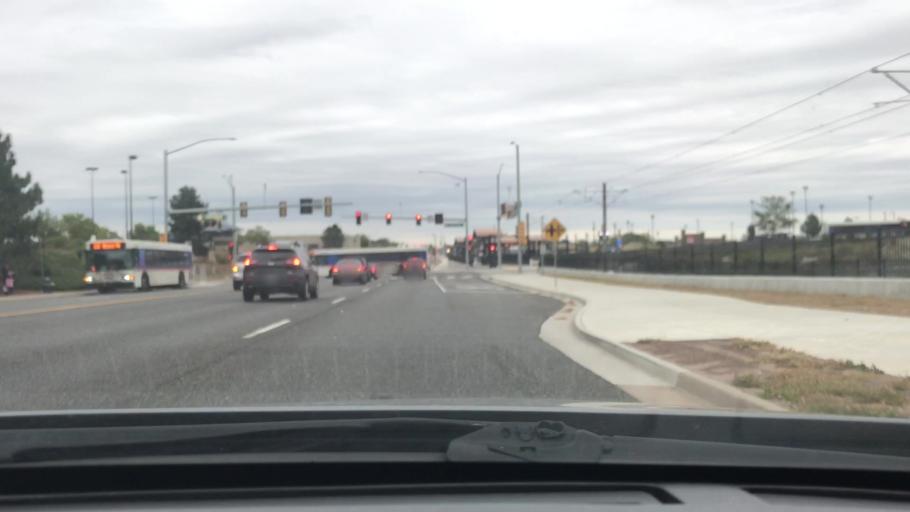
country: US
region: Colorado
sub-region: Adams County
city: Aurora
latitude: 39.7070
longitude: -104.8192
